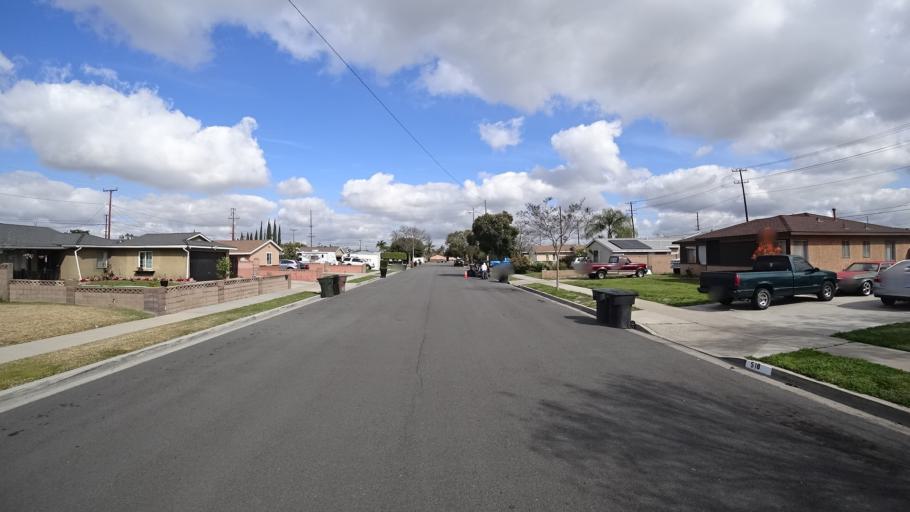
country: US
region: California
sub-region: Orange County
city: Buena Park
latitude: 33.8382
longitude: -117.9726
